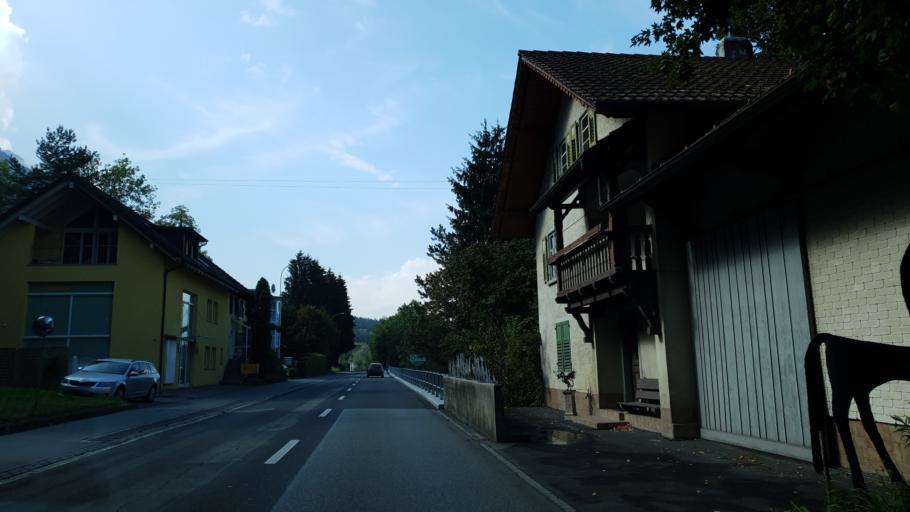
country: LI
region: Mauren
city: Mauren
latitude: 47.2156
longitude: 9.5657
